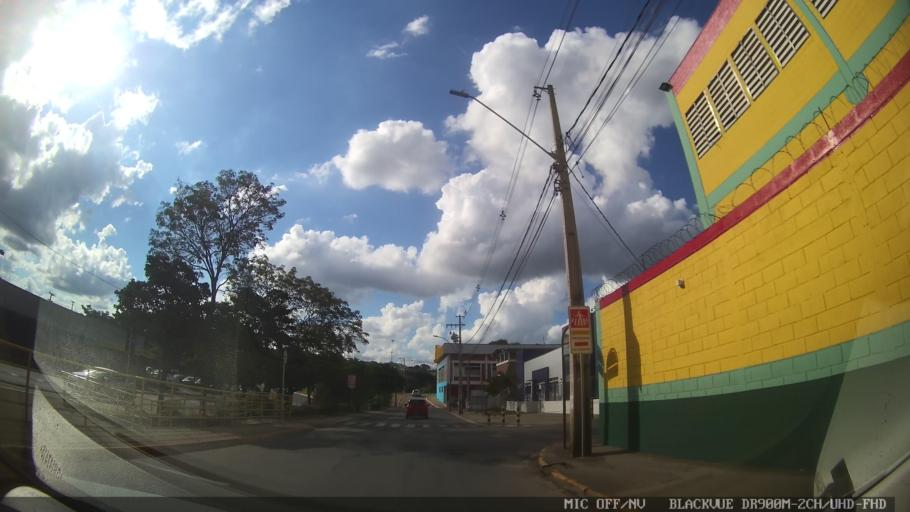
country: BR
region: Minas Gerais
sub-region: Extrema
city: Extrema
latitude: -22.8564
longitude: -46.3244
